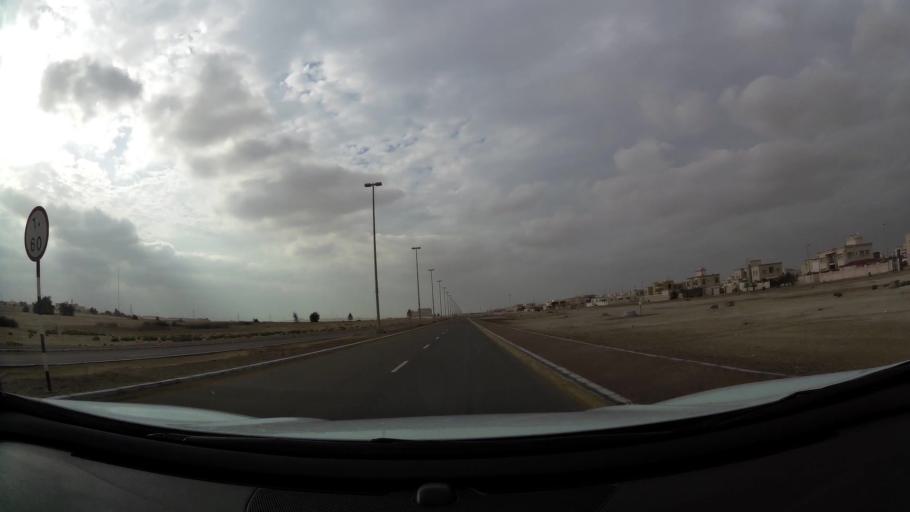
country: AE
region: Abu Dhabi
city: Abu Dhabi
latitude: 24.3359
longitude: 54.6239
